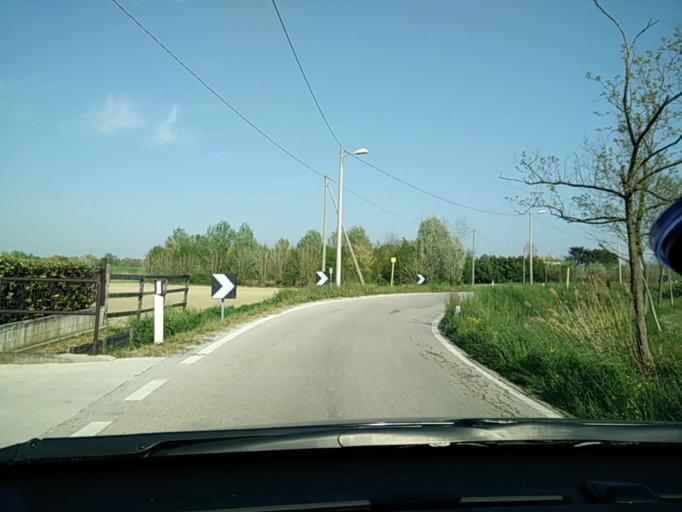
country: IT
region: Veneto
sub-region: Provincia di Venezia
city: Dese
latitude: 45.5255
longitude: 12.3127
